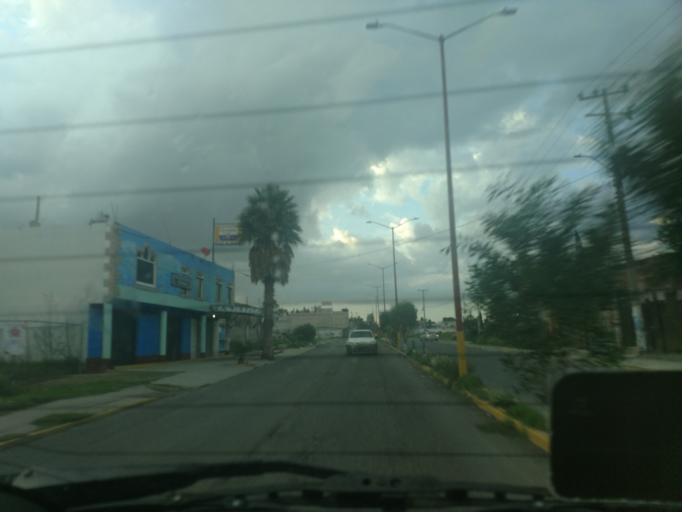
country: MX
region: Morelos
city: Coyotepec
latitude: 19.7661
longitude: -99.2013
